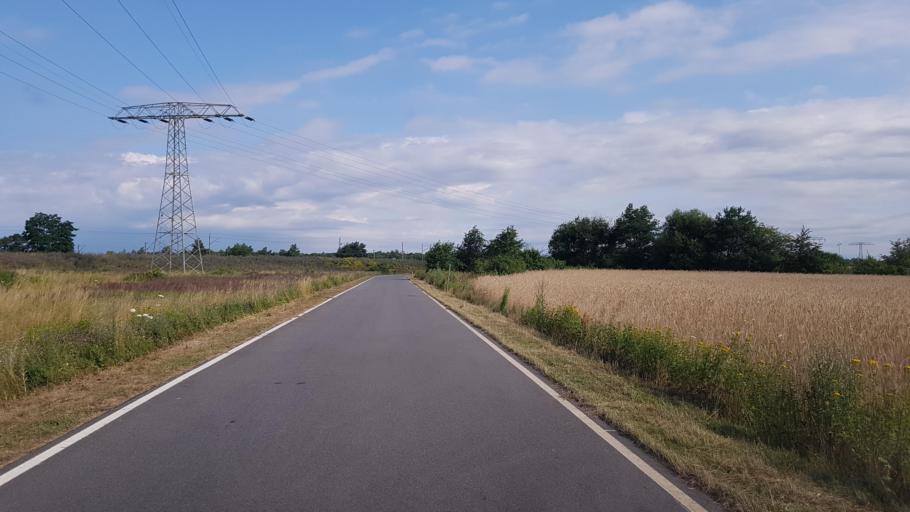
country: DE
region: Brandenburg
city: Grossraschen
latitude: 51.5568
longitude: 14.0613
